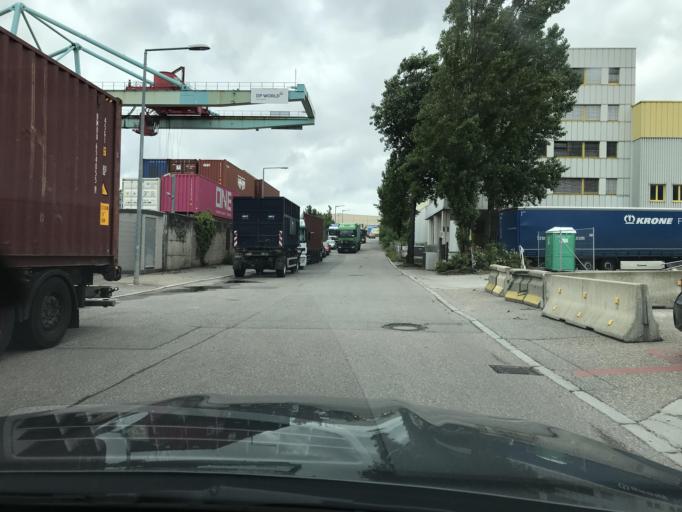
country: DE
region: Baden-Wuerttemberg
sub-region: Regierungsbezirk Stuttgart
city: Fellbach
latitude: 48.7699
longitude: 9.2585
